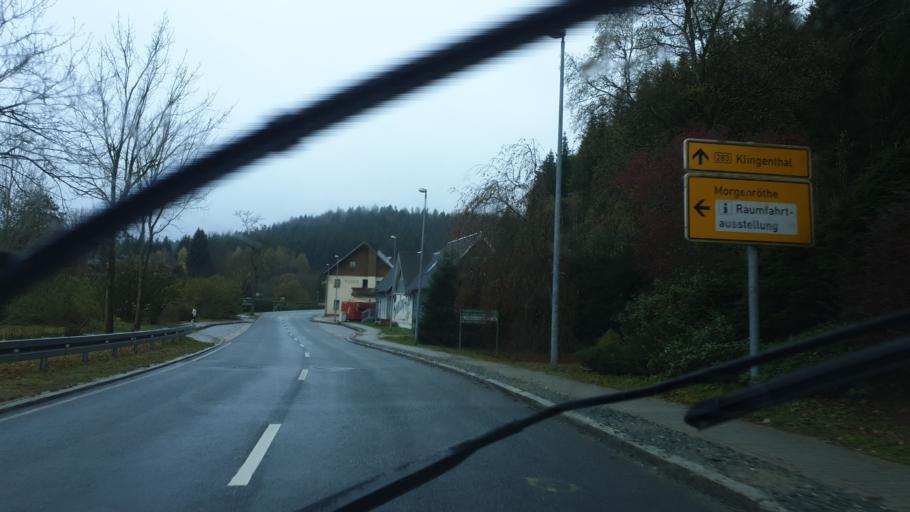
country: DE
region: Saxony
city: Muldenhammer
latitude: 50.4613
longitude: 12.4902
